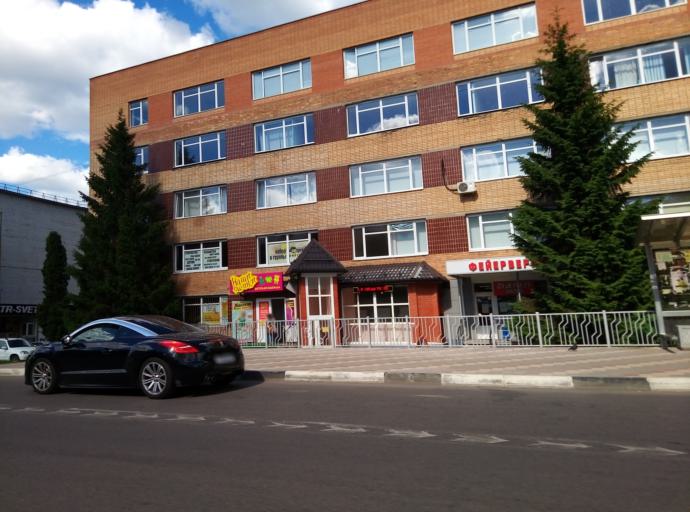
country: RU
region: Kursk
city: Kursk
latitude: 51.7590
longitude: 36.1873
